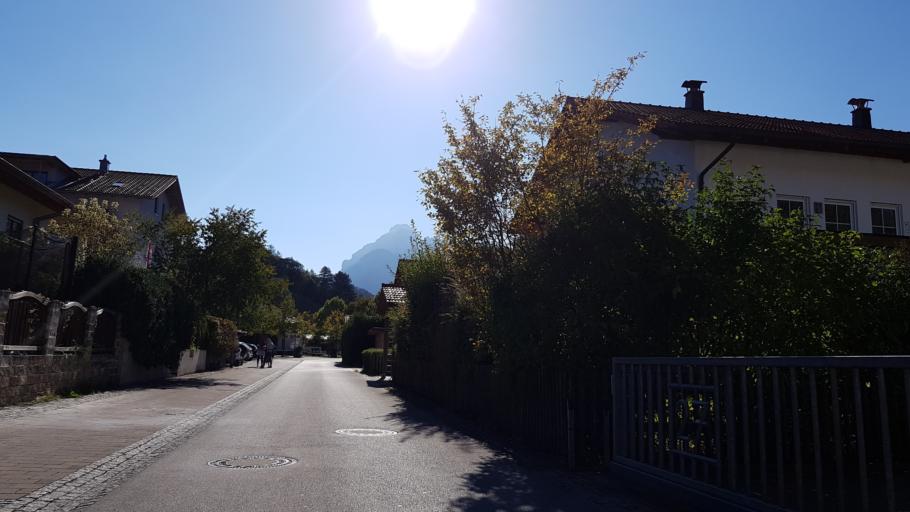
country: DE
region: Bavaria
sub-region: Swabia
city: Fuessen
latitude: 47.5741
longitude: 10.6890
